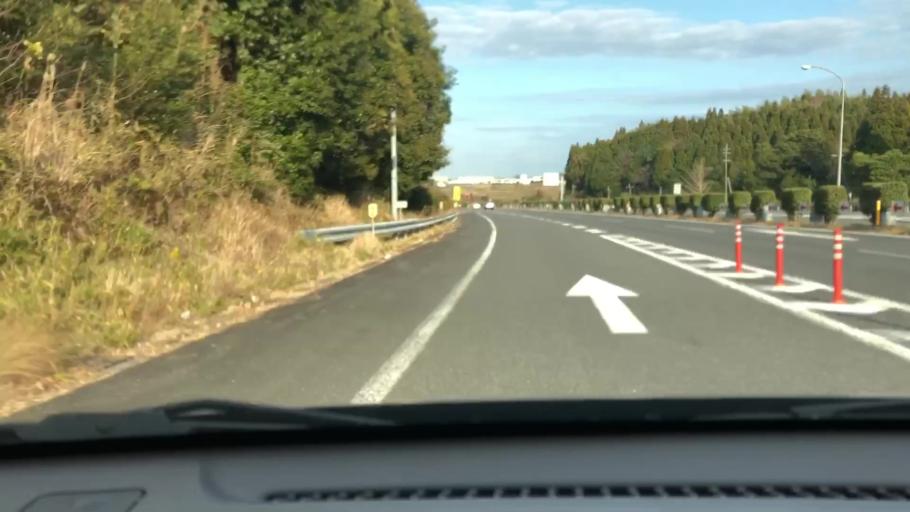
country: JP
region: Miyazaki
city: Miyazaki-shi
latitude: 31.8223
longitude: 131.3044
